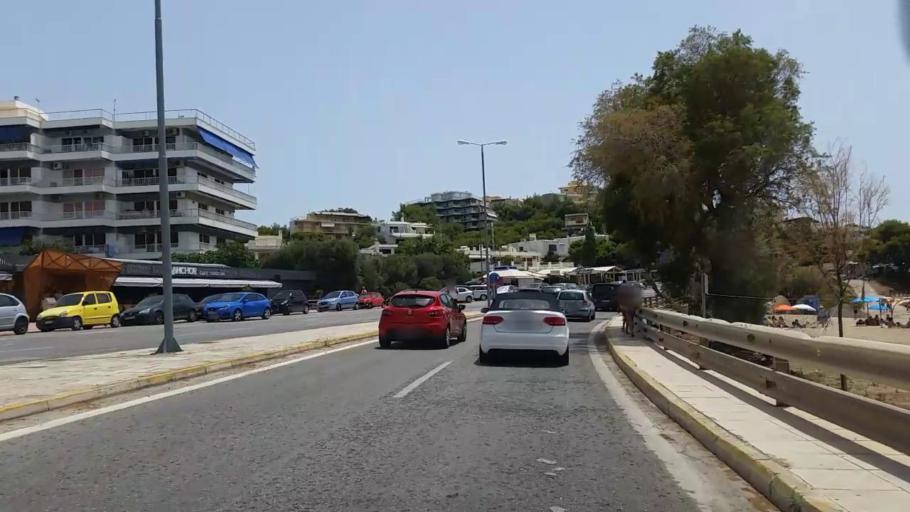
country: GR
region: Attica
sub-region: Nomarchia Anatolikis Attikis
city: Saronida
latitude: 37.7486
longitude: 23.9054
